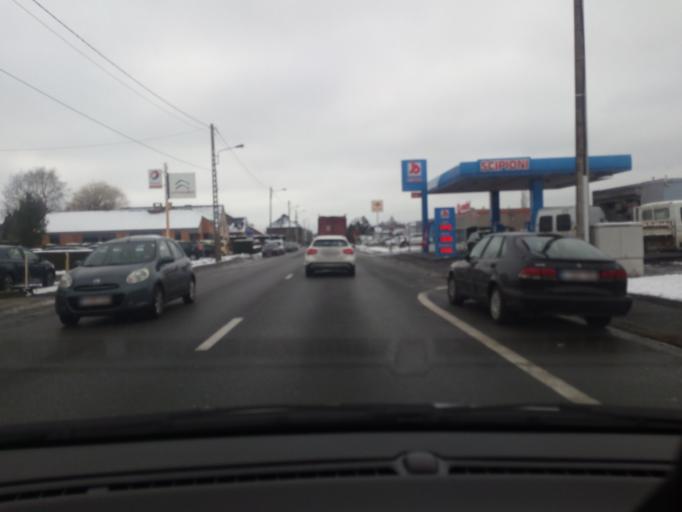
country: BE
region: Wallonia
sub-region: Province du Hainaut
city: Frameries
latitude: 50.4084
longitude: 3.8854
